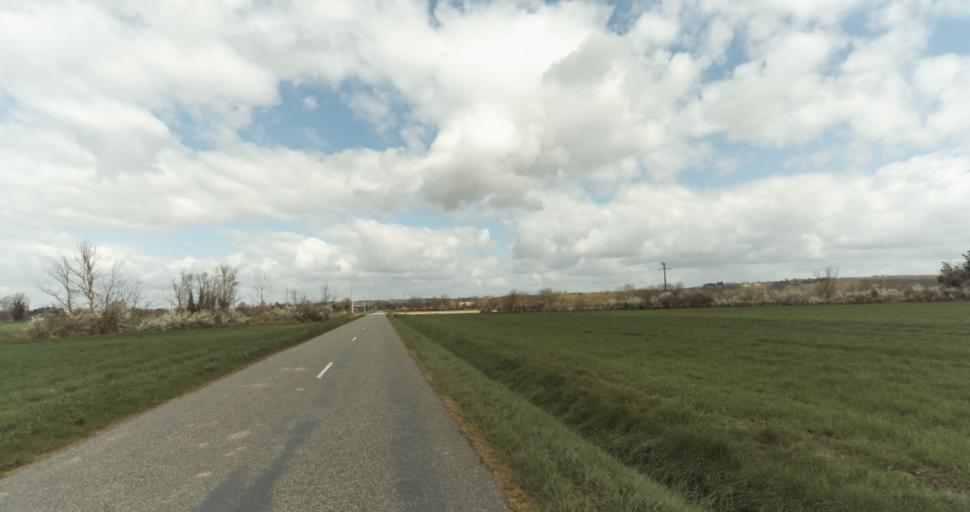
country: FR
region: Midi-Pyrenees
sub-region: Departement de la Haute-Garonne
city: Auterive
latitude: 43.3275
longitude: 1.4773
